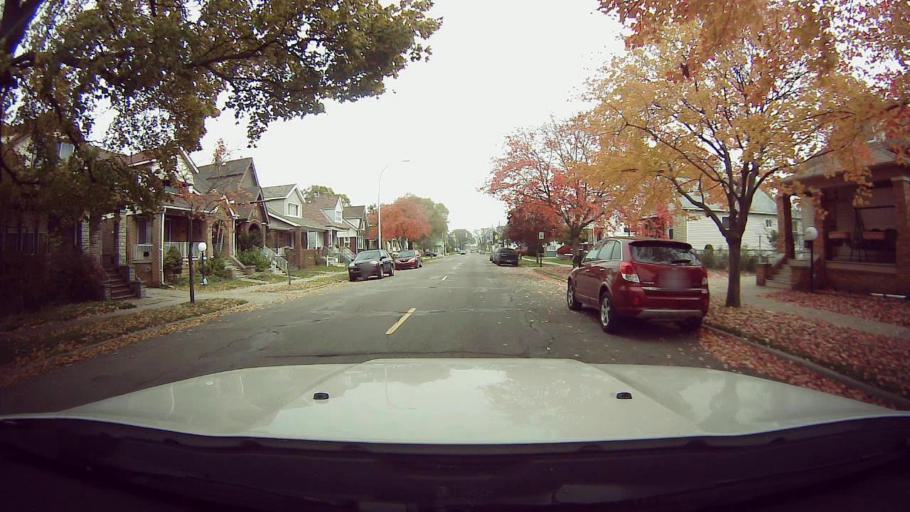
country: US
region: Michigan
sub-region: Wayne County
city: Hamtramck
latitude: 42.4039
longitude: -83.0486
